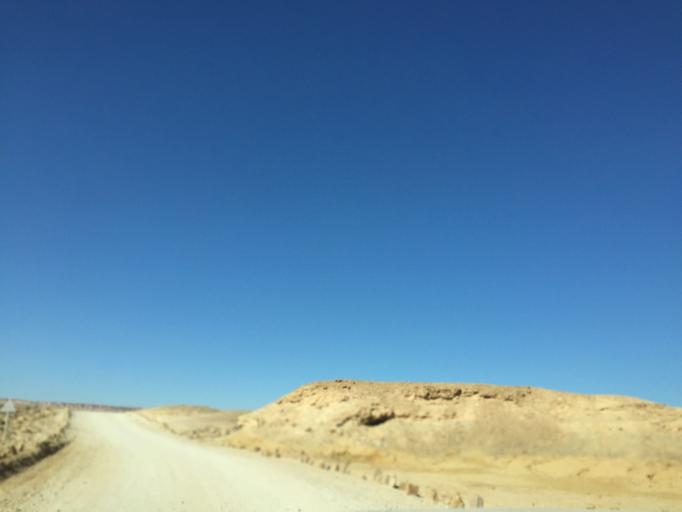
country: IL
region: Southern District
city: Mitzpe Ramon
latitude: 30.6132
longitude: 34.9333
